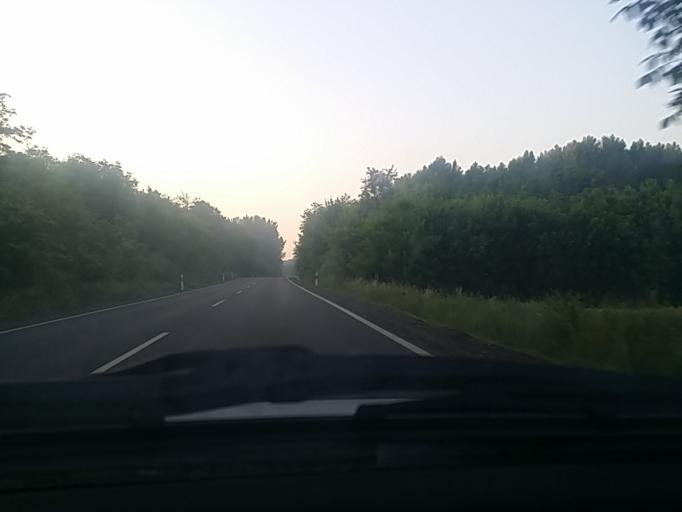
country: HU
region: Pest
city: Gyomro
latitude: 47.4370
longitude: 19.4083
